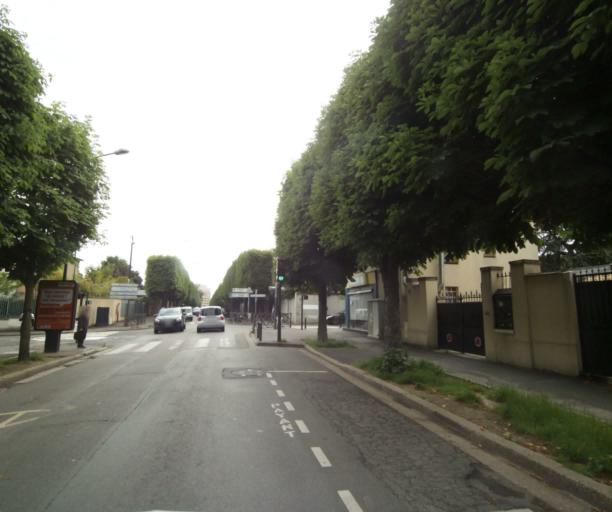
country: FR
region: Ile-de-France
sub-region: Departement du Val-d'Oise
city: Argenteuil
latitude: 48.9444
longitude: 2.2453
